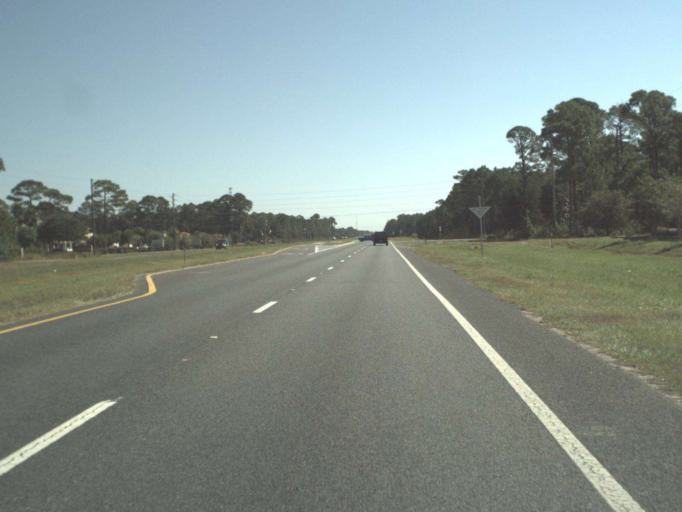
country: US
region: Florida
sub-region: Walton County
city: Miramar Beach
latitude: 30.3744
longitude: -86.2567
